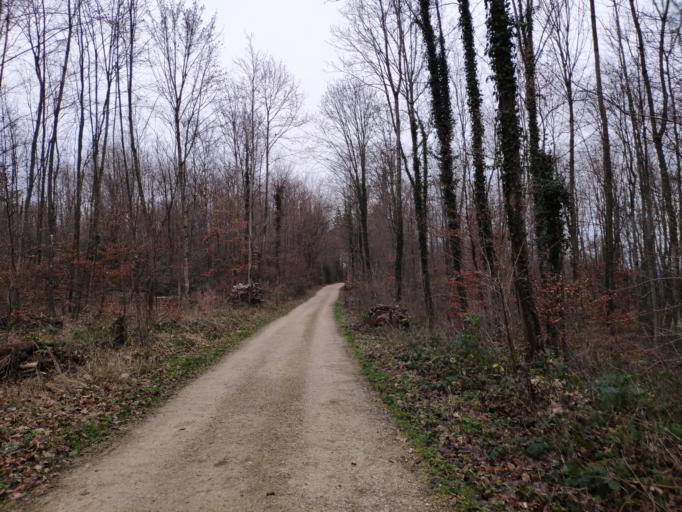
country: CH
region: Basel-City
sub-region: Basel-Stadt
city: Bettingen
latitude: 47.5747
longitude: 7.6772
